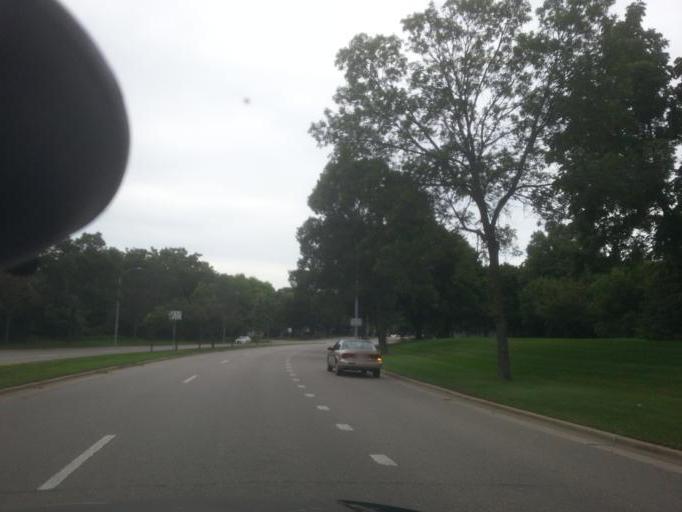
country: US
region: Wisconsin
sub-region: Dane County
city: Shorewood Hills
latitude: 43.0627
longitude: -89.4723
